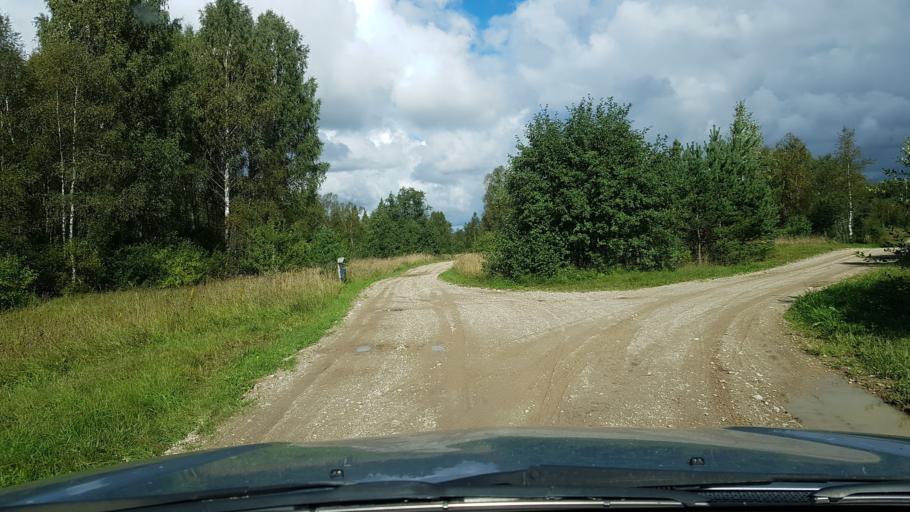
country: EE
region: Harju
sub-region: Raasiku vald
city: Arukula
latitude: 59.3113
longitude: 25.0741
